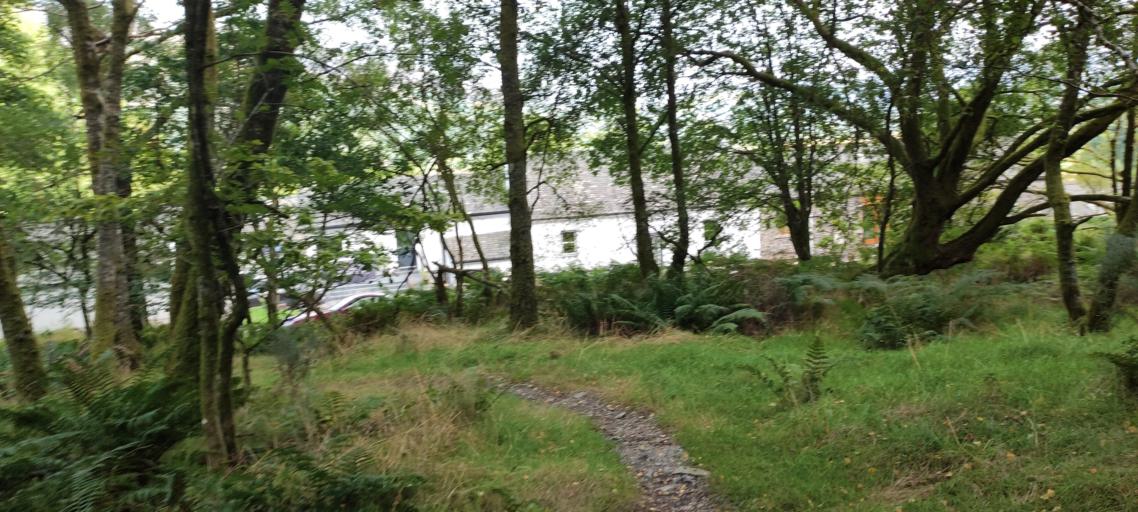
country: GB
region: England
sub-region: Cumbria
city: Keswick
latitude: 54.6257
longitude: -3.2105
